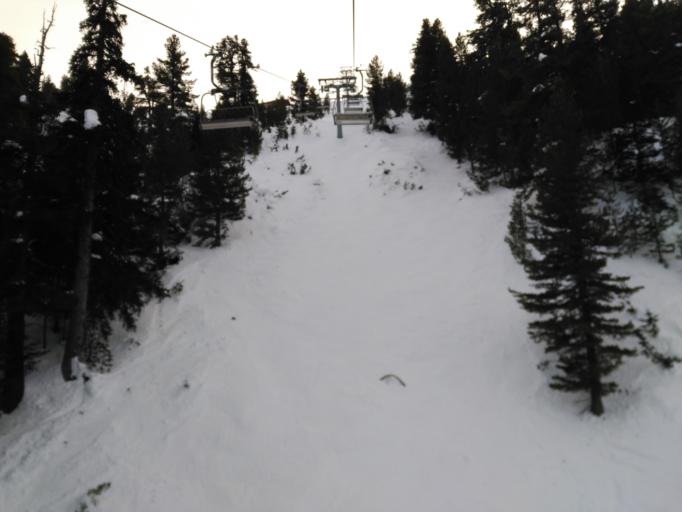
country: BG
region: Blagoevgrad
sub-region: Obshtina Bansko
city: Bansko
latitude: 41.7644
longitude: 23.4482
